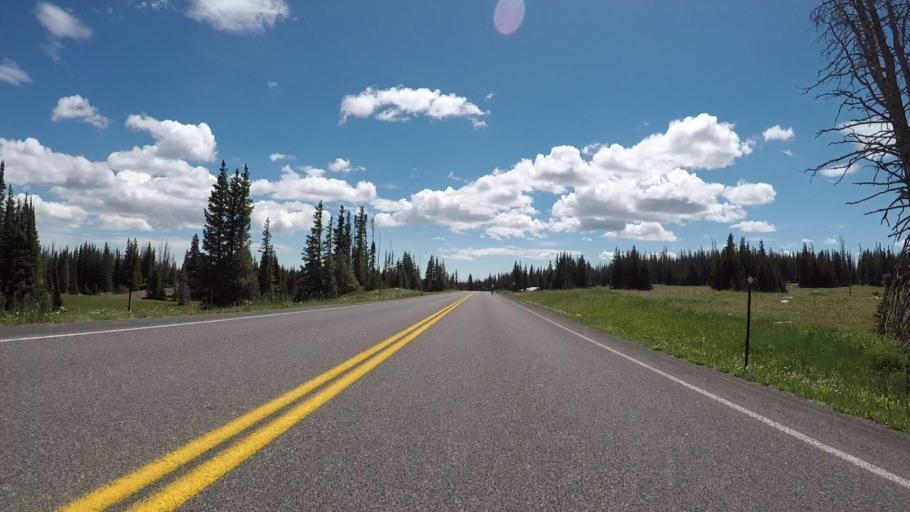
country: US
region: Wyoming
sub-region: Carbon County
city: Saratoga
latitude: 41.3518
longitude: -106.2611
